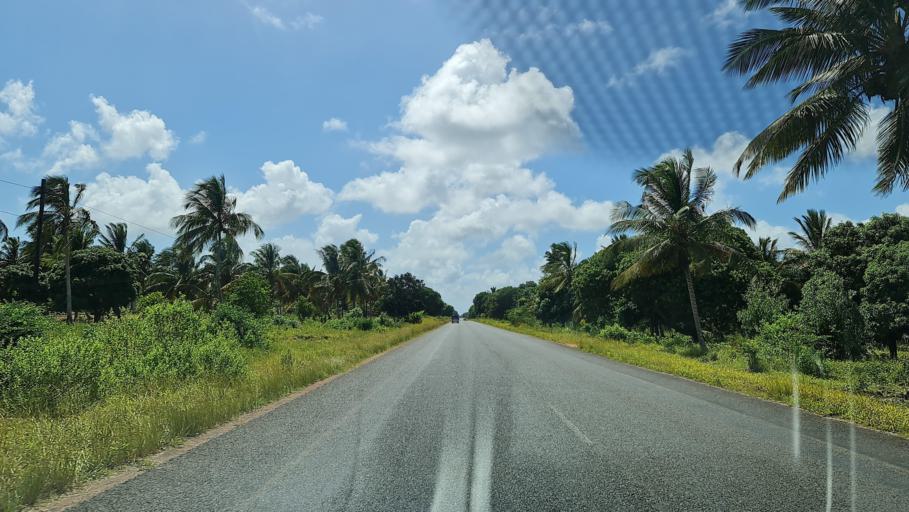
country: MZ
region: Inhambane
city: Maxixe
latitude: -24.5419
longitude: 34.9051
